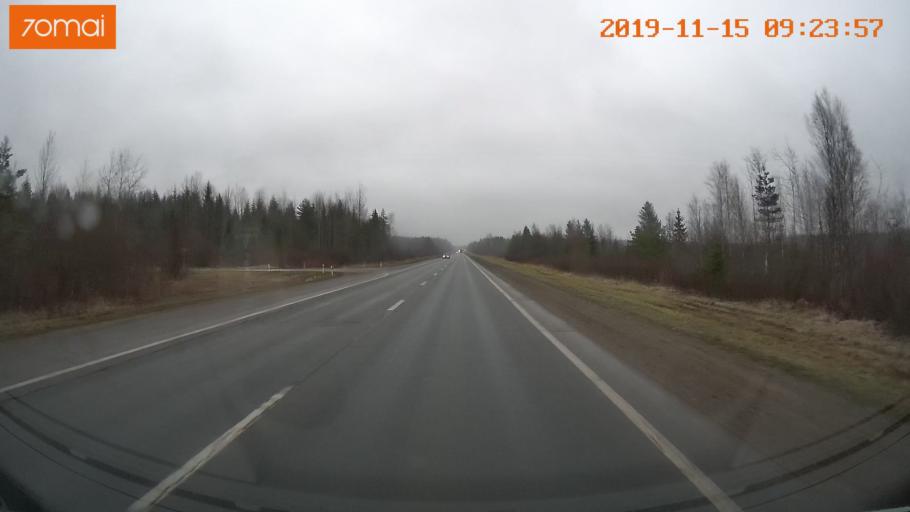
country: RU
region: Vologda
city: Tonshalovo
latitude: 59.3026
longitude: 38.1253
